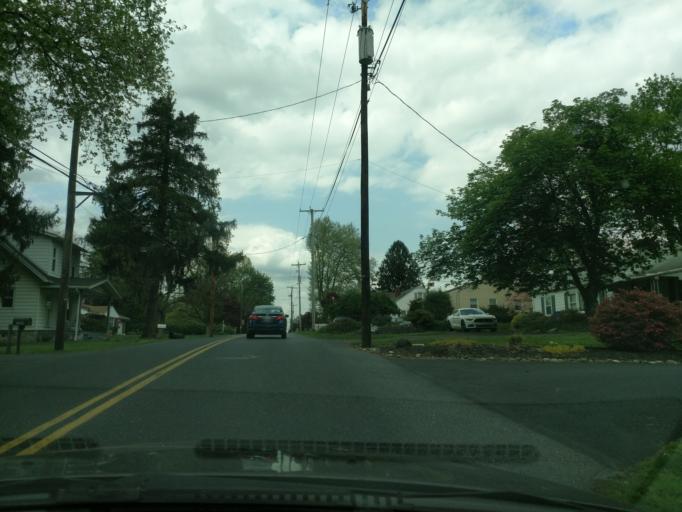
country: US
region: Pennsylvania
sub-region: Lebanon County
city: Lebanon South
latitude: 40.3255
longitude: -76.4107
